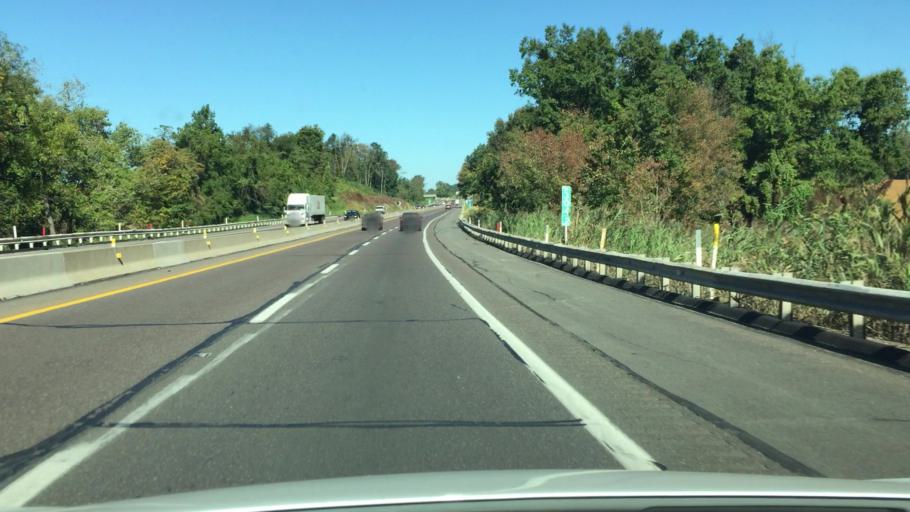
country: US
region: Pennsylvania
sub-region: Chester County
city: Elverson
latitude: 40.1266
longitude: -75.7862
